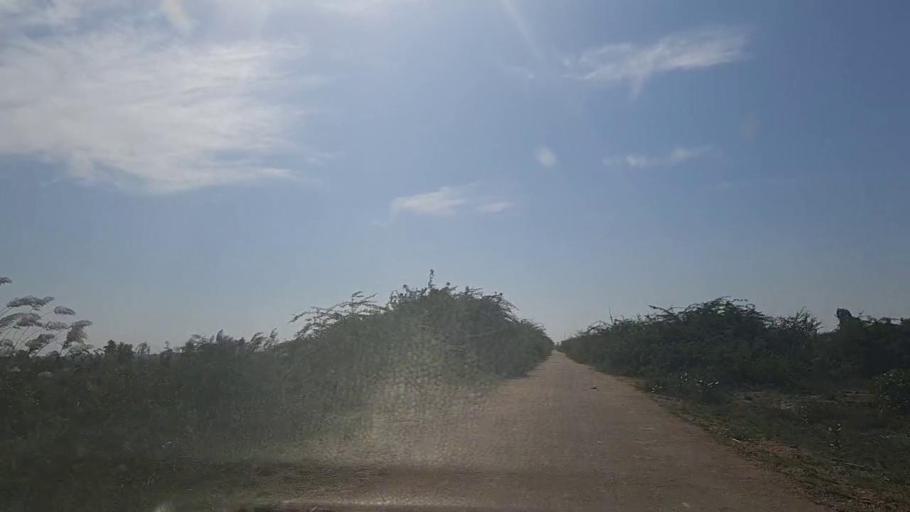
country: PK
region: Sindh
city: Mirpur Batoro
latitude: 24.6759
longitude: 68.1827
